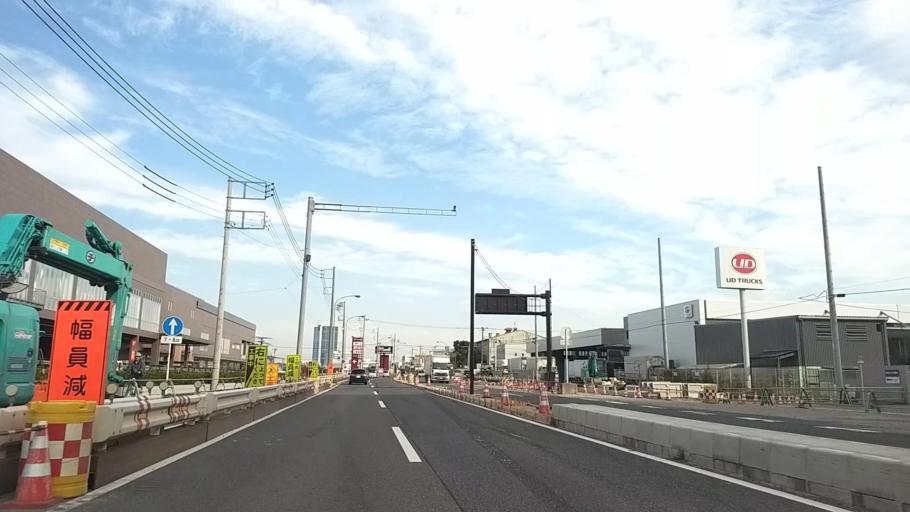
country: JP
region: Kanagawa
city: Atsugi
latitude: 35.4087
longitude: 139.3616
